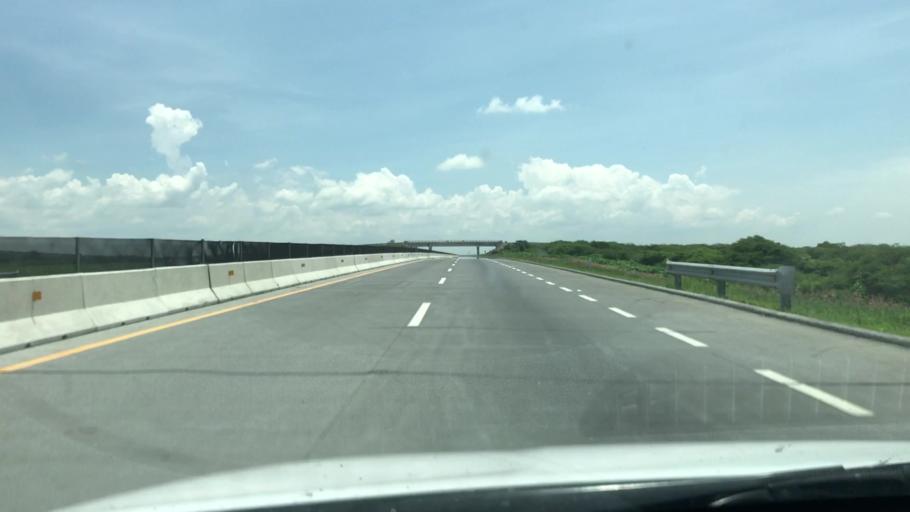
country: MX
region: Jalisco
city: Degollado
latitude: 20.3843
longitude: -102.1166
